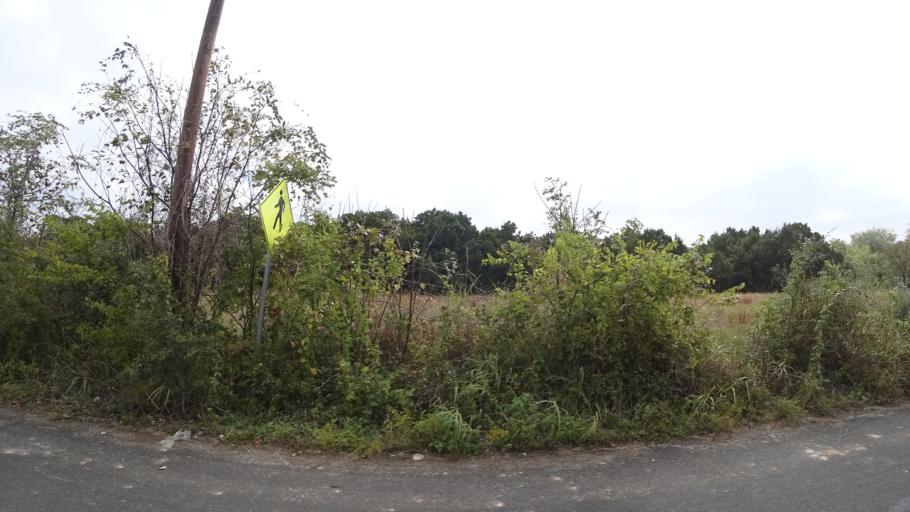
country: US
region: Texas
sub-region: Travis County
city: Shady Hollow
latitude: 30.2069
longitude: -97.8294
